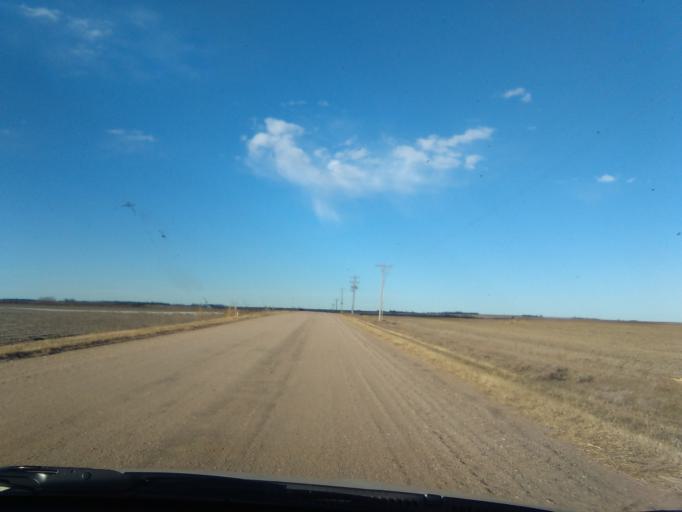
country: US
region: Nebraska
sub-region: Kearney County
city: Minden
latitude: 40.3118
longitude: -98.7457
